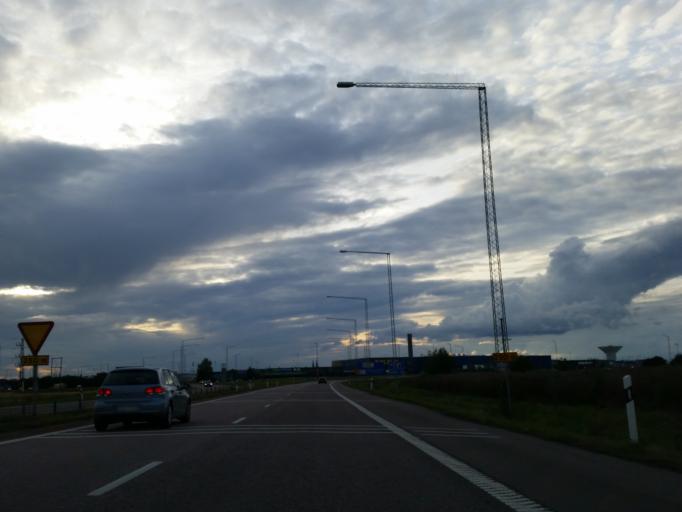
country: SE
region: Uppsala
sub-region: Uppsala Kommun
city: Saevja
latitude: 59.8438
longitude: 17.7063
